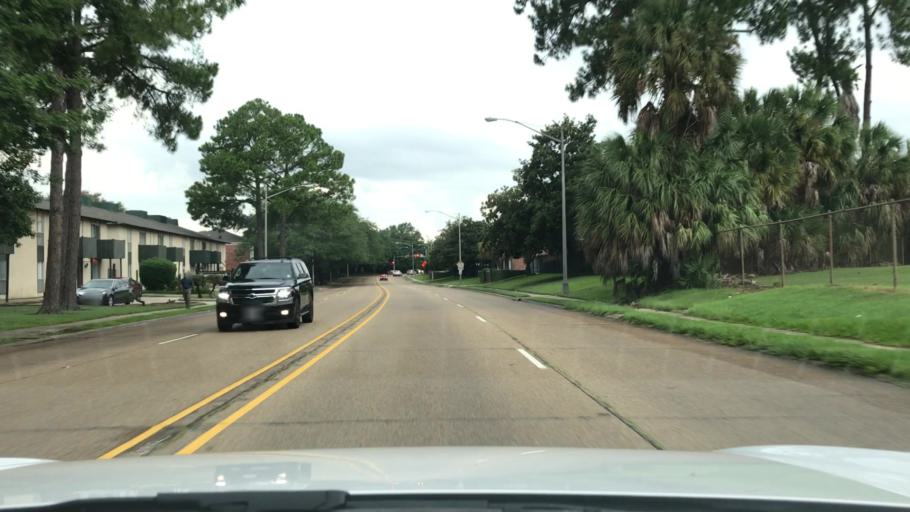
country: US
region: Louisiana
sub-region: East Baton Rouge Parish
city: Baton Rouge
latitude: 30.4400
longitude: -91.1355
